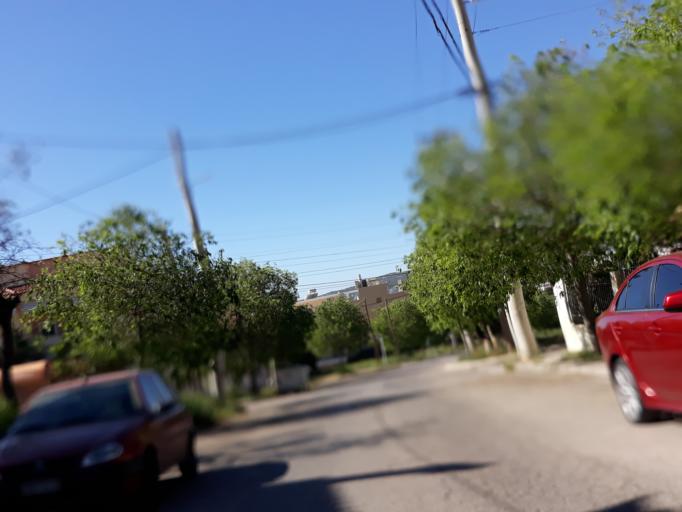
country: GR
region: Attica
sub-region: Nomarchia Dytikis Attikis
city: Ano Liosia
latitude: 38.0941
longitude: 23.7114
